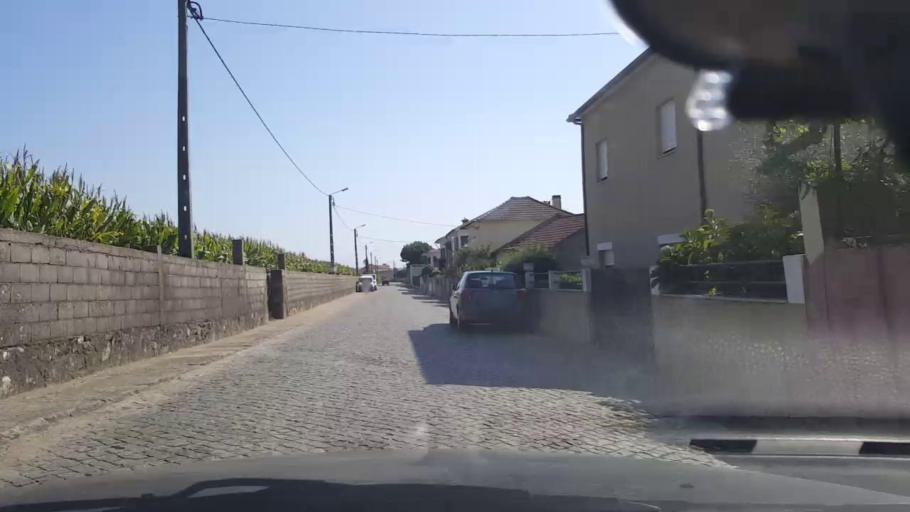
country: PT
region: Porto
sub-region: Povoa de Varzim
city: Pedroso
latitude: 41.4097
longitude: -8.6939
